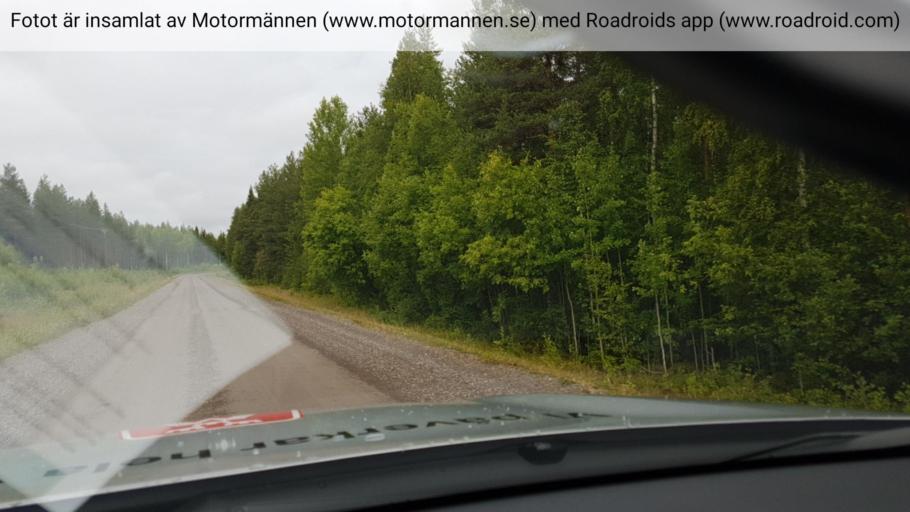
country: SE
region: Norrbotten
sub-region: Alvsbyns Kommun
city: AElvsbyn
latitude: 66.0254
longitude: 21.0163
